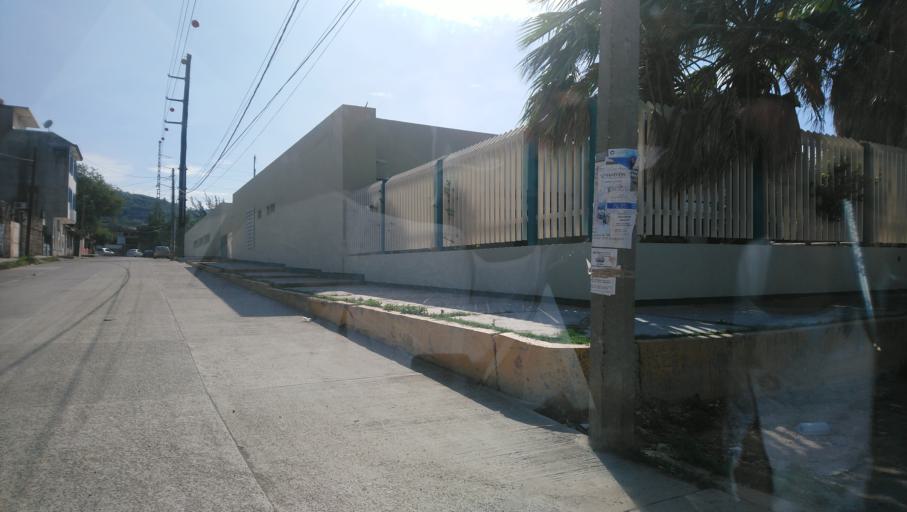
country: MX
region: Oaxaca
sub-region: Salina Cruz
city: Salina Cruz
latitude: 16.2020
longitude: -95.2010
